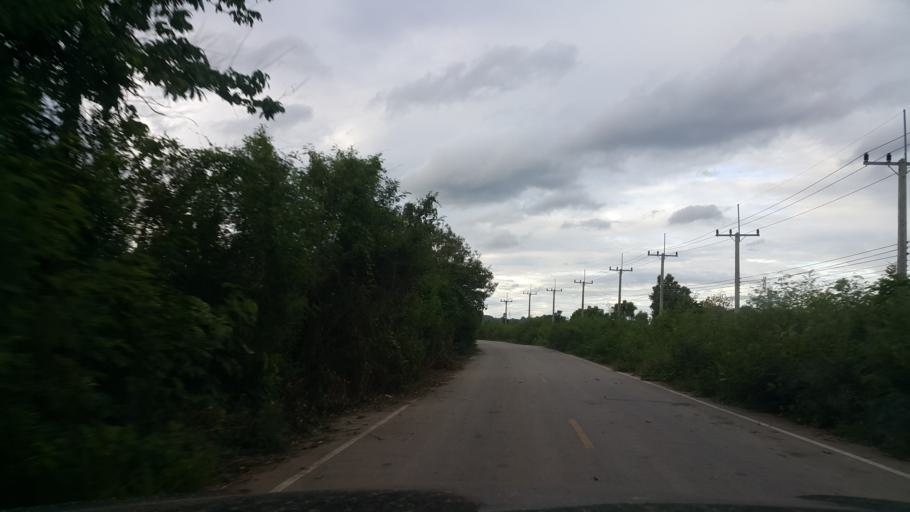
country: TH
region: Sukhothai
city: Ban Dan Lan Hoi
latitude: 17.1615
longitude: 99.5238
